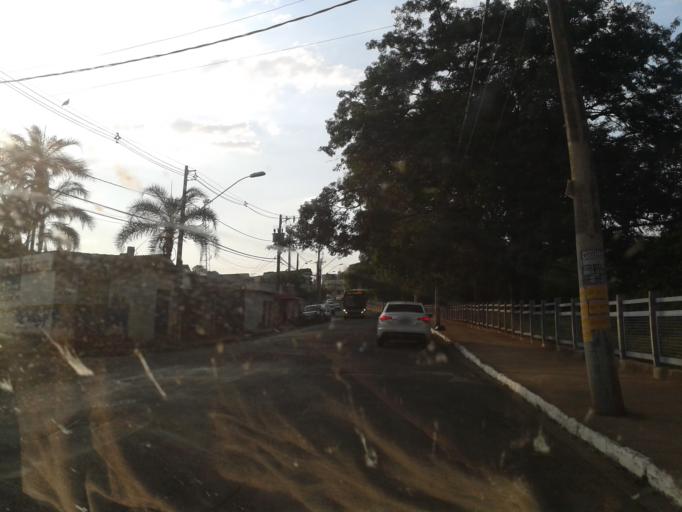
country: BR
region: Minas Gerais
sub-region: Uberlandia
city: Uberlandia
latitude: -18.9193
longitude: -48.3253
